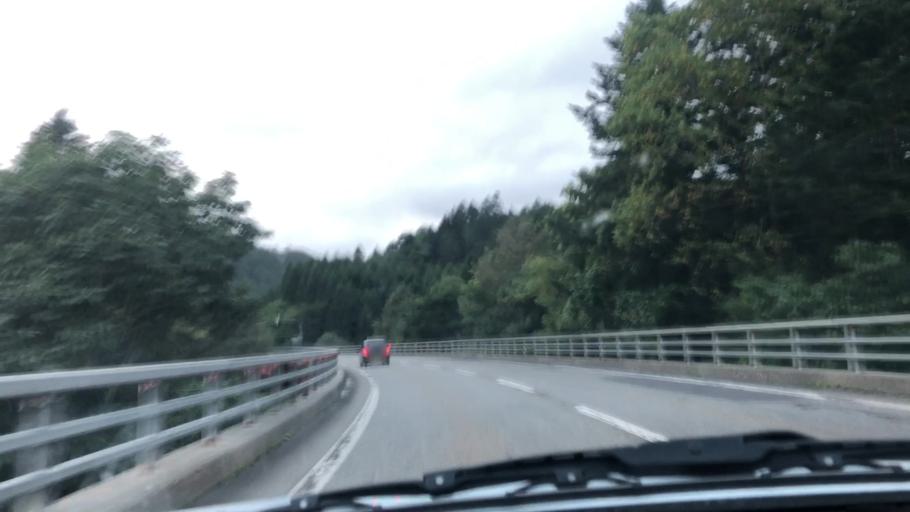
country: JP
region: Hokkaido
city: Iwamizawa
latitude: 42.9084
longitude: 142.1259
